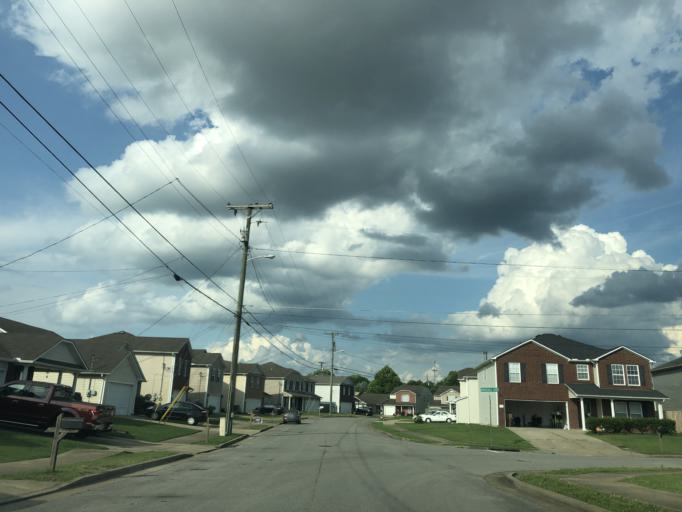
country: US
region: Tennessee
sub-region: Davidson County
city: Nashville
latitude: 36.2342
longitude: -86.7950
